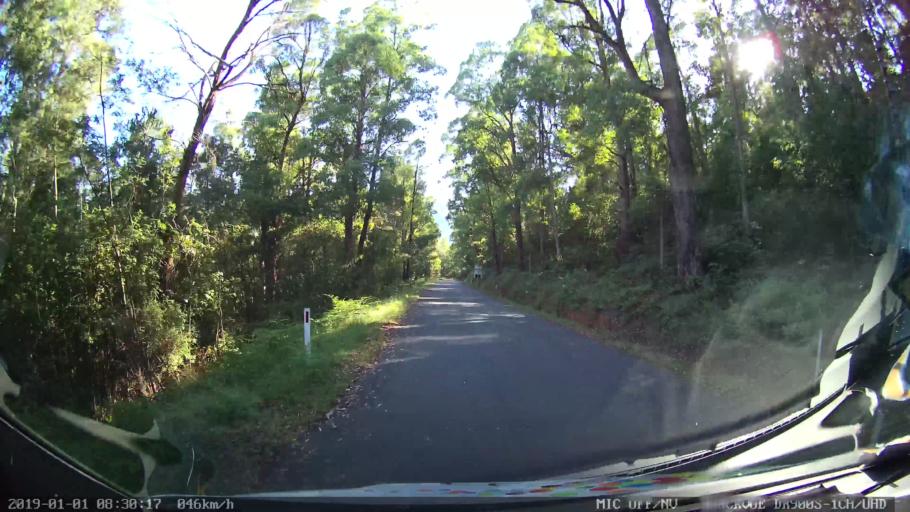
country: AU
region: New South Wales
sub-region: Snowy River
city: Jindabyne
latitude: -36.3766
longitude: 148.1970
